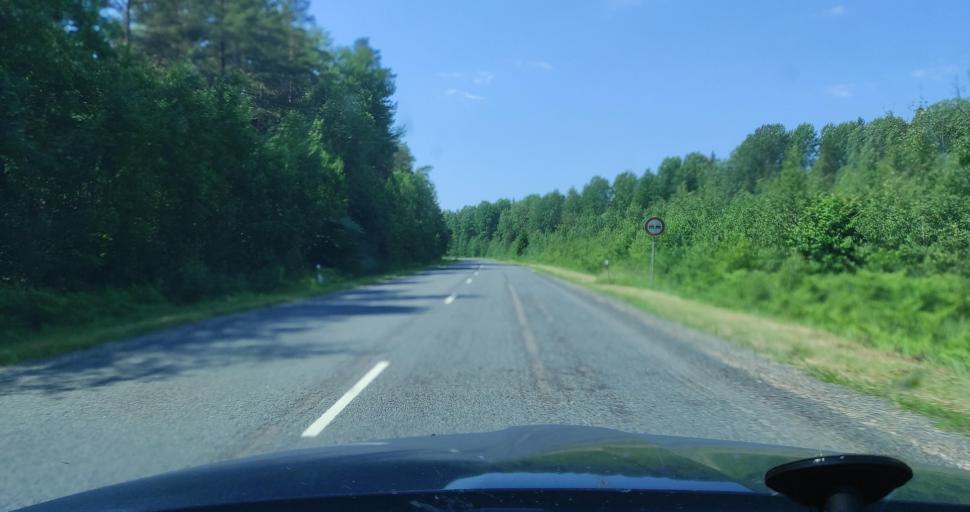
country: LV
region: Salacgrivas
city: Ainazi
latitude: 57.8597
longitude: 24.4896
